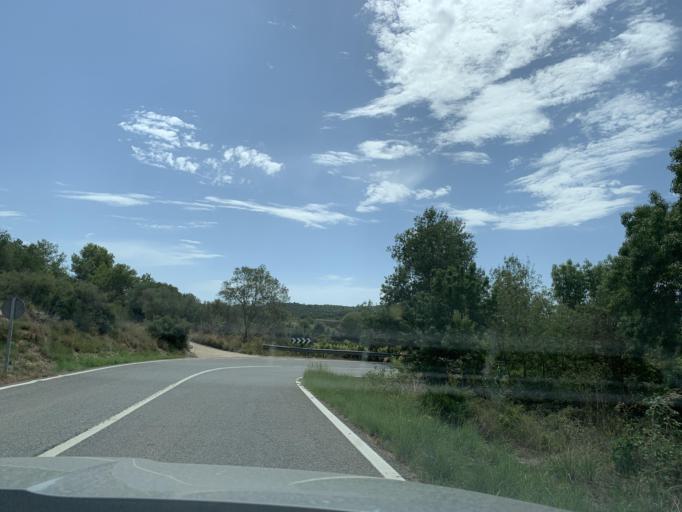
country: ES
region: Catalonia
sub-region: Provincia de Tarragona
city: Altafulla
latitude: 41.1622
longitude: 1.3659
